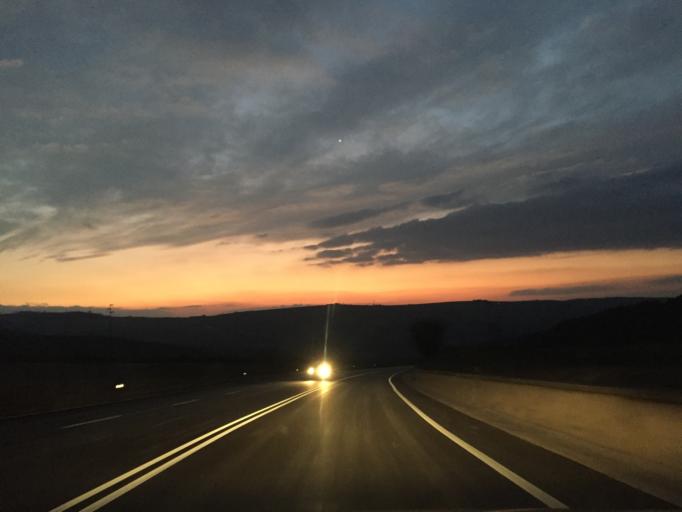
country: IT
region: Apulia
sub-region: Provincia di Foggia
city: Volturino
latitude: 41.4561
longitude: 15.0832
